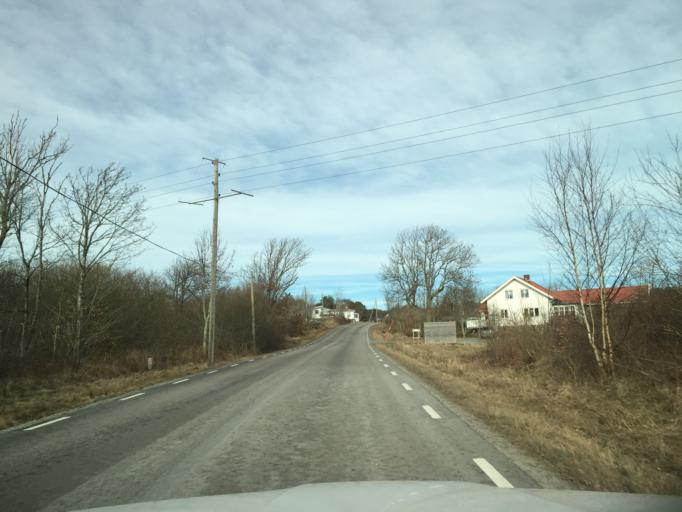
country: SE
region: Vaestra Goetaland
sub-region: Tjorns Kommun
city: Skaerhamn
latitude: 58.0198
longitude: 11.5332
